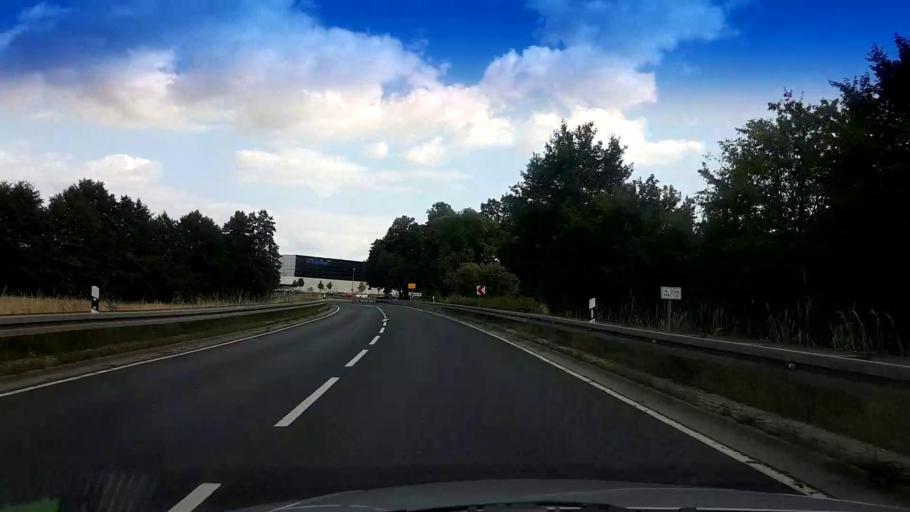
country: DE
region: Bavaria
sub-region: Upper Franconia
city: Baunach
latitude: 49.9922
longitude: 10.8420
